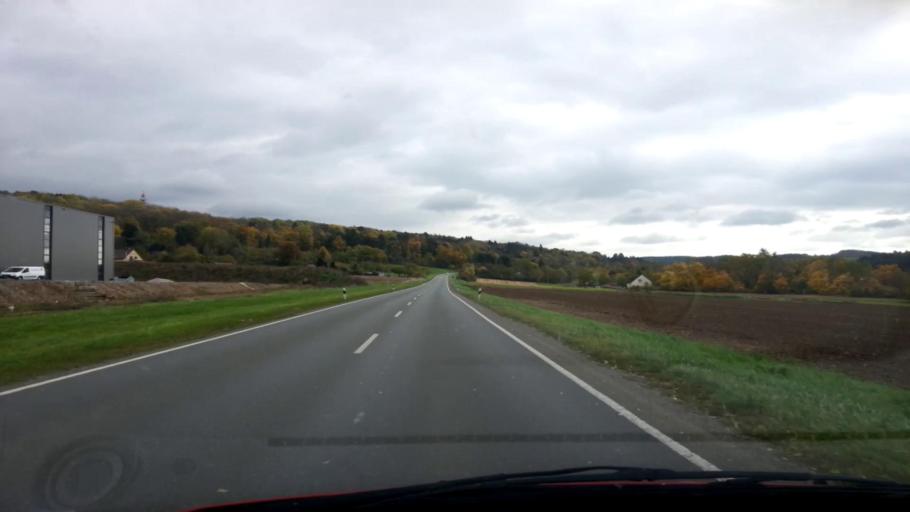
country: DE
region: Bavaria
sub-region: Upper Franconia
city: Bindlach
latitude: 49.9634
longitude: 11.6286
